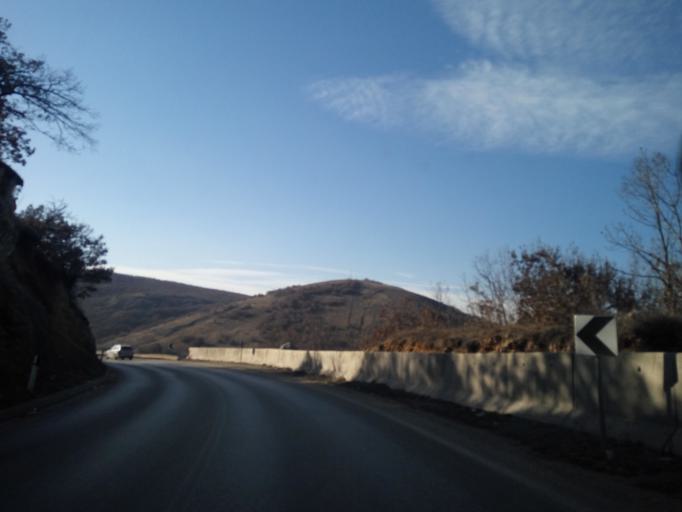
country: XK
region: Pristina
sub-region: Komuna e Prishtines
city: Pristina
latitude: 42.6187
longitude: 21.2249
